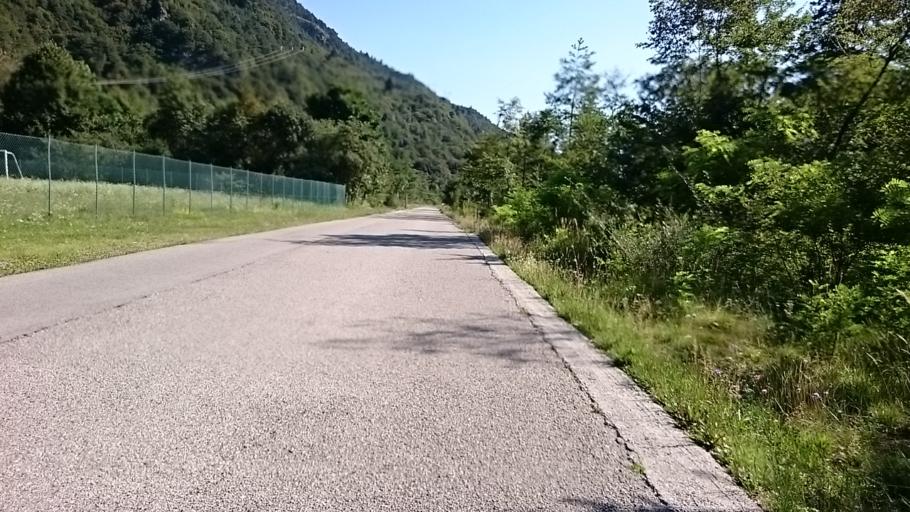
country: IT
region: Veneto
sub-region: Provincia di Belluno
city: Longarone
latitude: 46.2395
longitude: 12.3075
